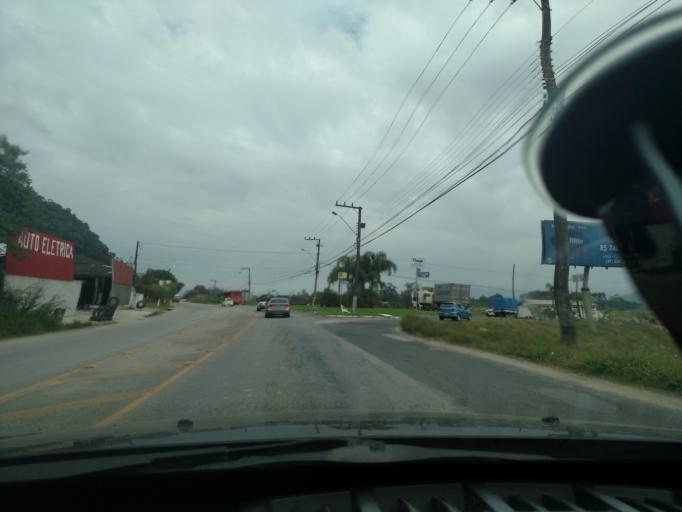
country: BR
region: Santa Catarina
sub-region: Itajai
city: Itajai
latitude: -26.8863
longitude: -48.7485
